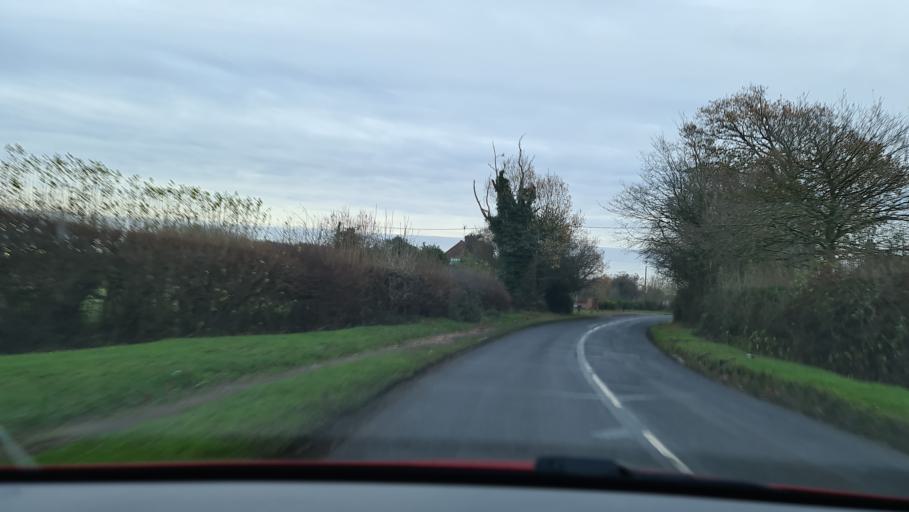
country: GB
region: England
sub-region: Buckinghamshire
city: Amersham on the Hill
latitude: 51.6880
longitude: -0.6253
